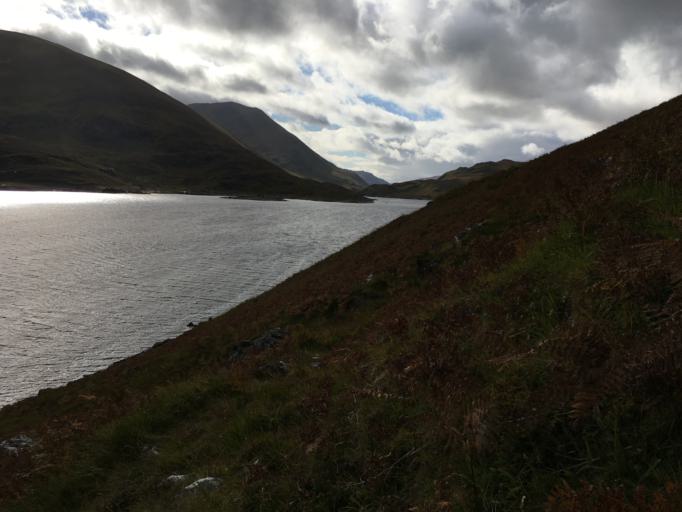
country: GB
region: Scotland
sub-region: Highland
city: Spean Bridge
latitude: 57.3316
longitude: -5.0476
